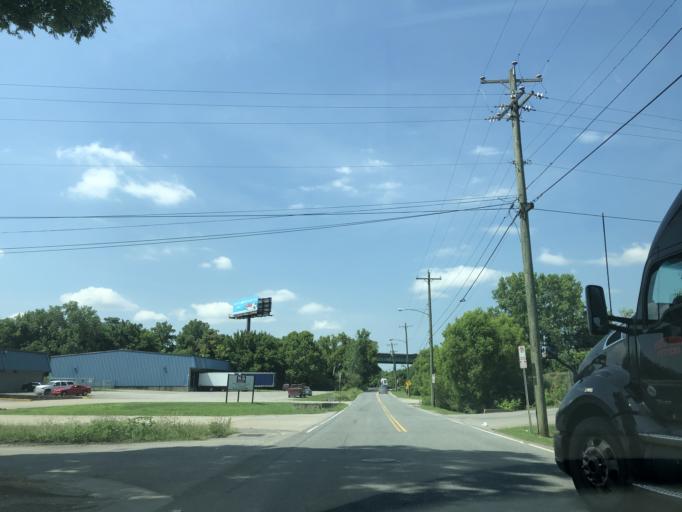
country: US
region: Tennessee
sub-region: Davidson County
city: Nashville
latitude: 36.1942
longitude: -86.7804
